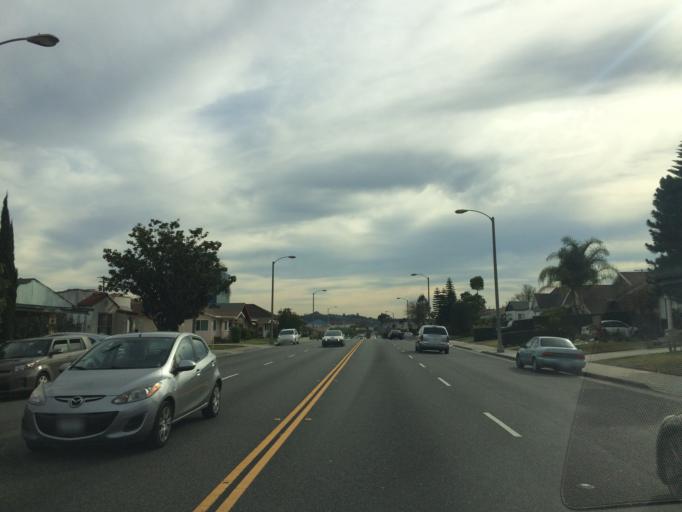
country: US
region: California
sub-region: Los Angeles County
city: Alhambra
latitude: 34.0904
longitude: -118.1521
